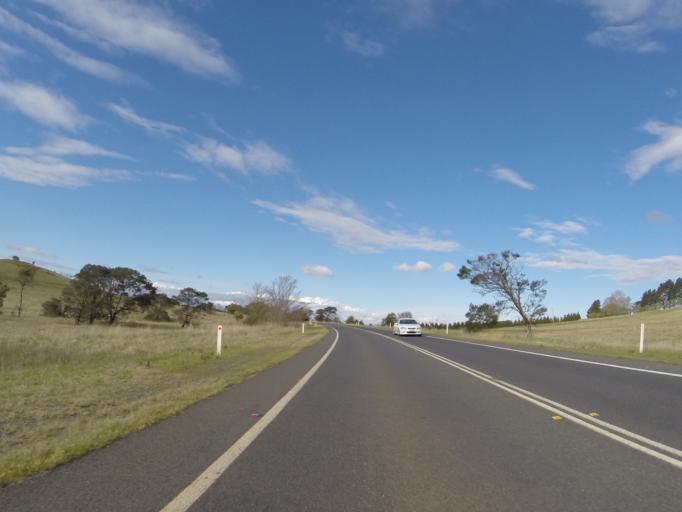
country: AU
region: New South Wales
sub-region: Wingecarribee
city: Bundanoon
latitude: -34.5870
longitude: 150.2925
